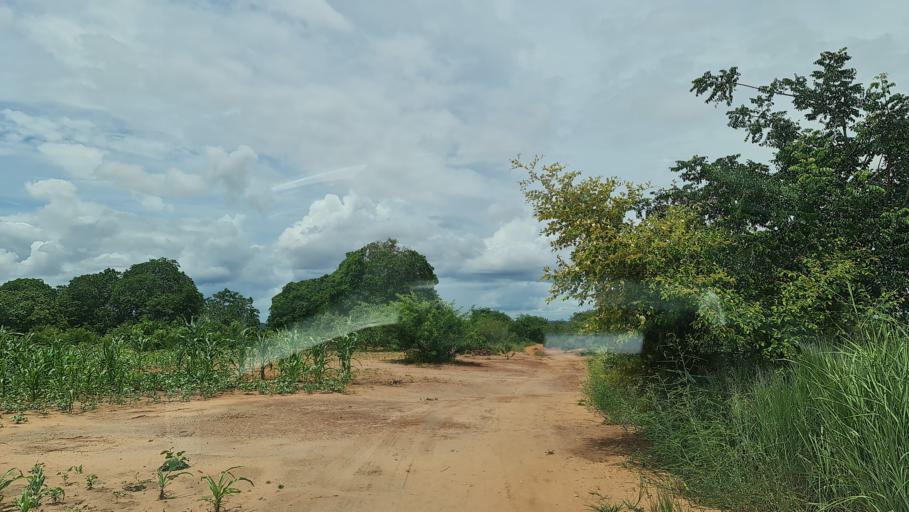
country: MZ
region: Nampula
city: Nacala
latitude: -14.7904
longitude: 39.9689
